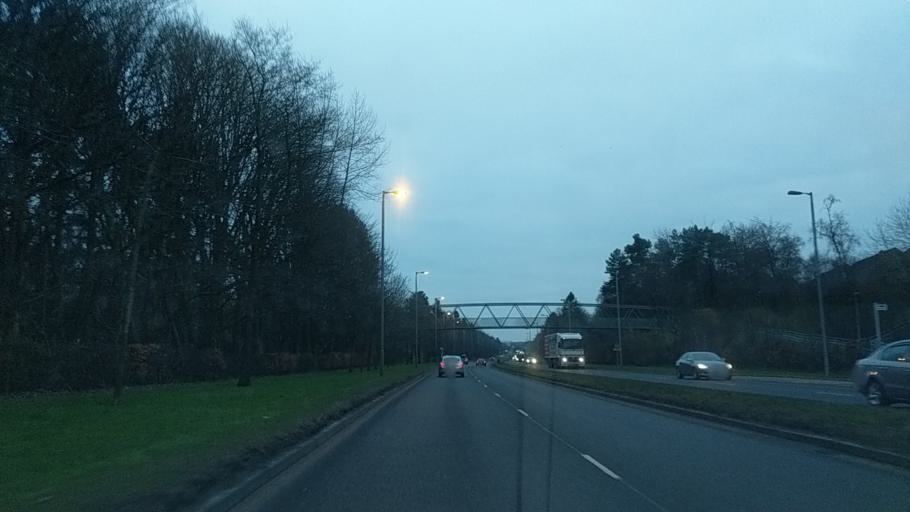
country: GB
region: Scotland
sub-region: South Lanarkshire
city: East Kilbride
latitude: 55.7739
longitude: -4.1634
